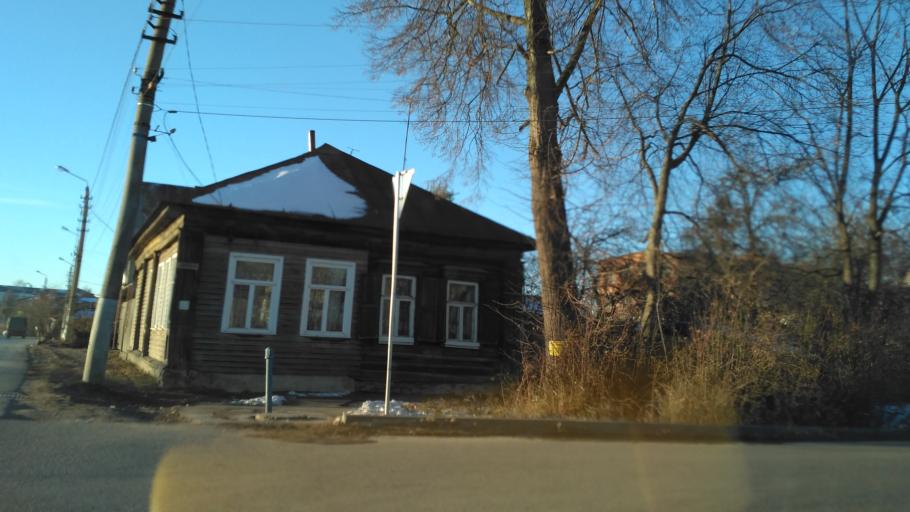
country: RU
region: Tula
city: Tula
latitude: 54.2056
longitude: 37.6075
